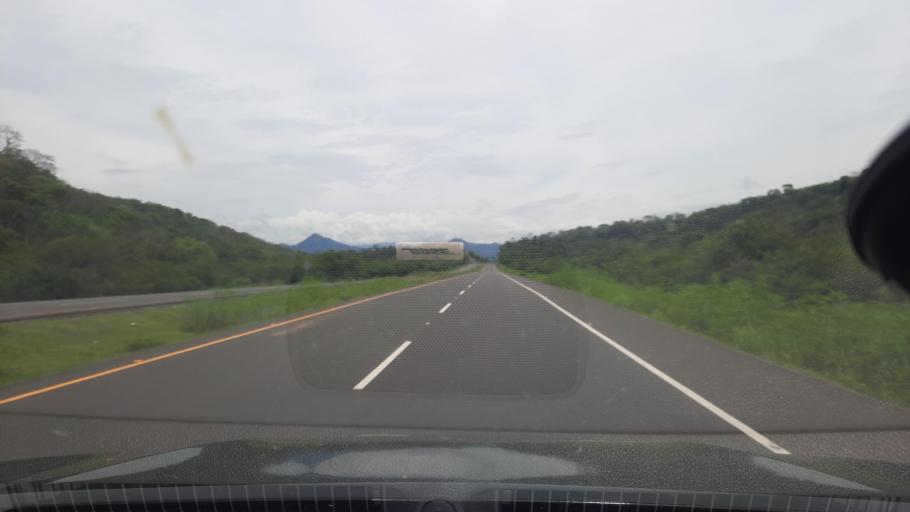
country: HN
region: Valle
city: Aramecina
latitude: 13.7301
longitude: -87.7170
